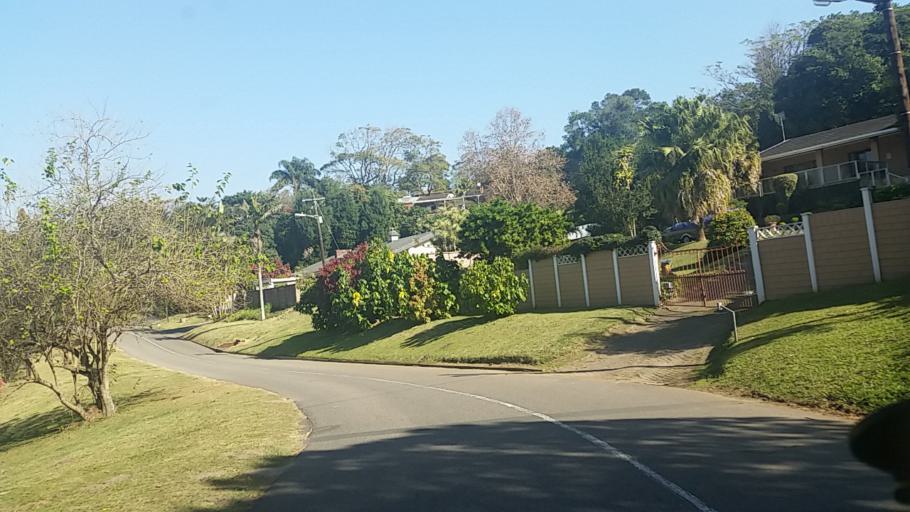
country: ZA
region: KwaZulu-Natal
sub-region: eThekwini Metropolitan Municipality
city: Berea
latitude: -29.8485
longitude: 30.9051
